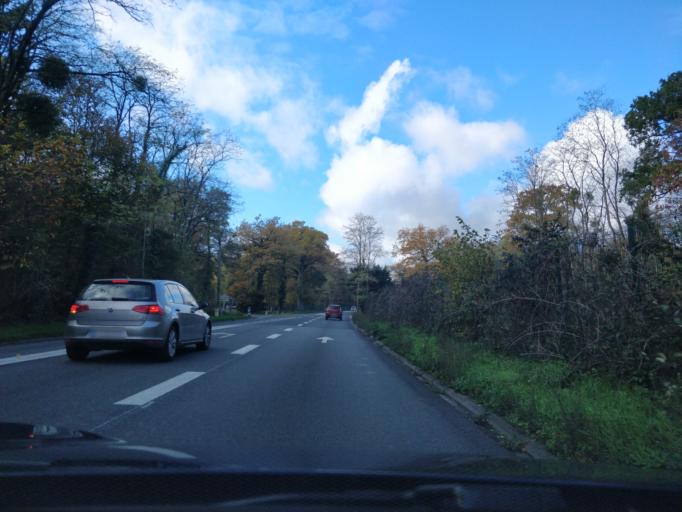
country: FR
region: Ile-de-France
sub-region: Departement de l'Essonne
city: Ollainville
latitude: 48.6037
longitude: 2.2095
